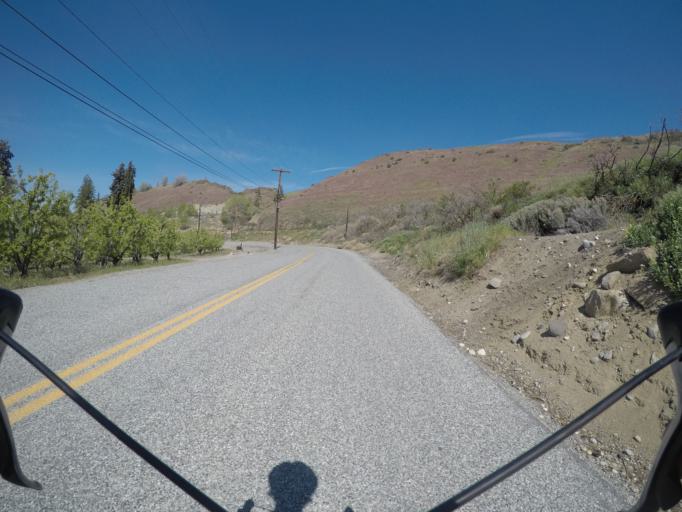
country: US
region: Washington
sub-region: Chelan County
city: Sunnyslope
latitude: 47.4706
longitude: -120.3537
